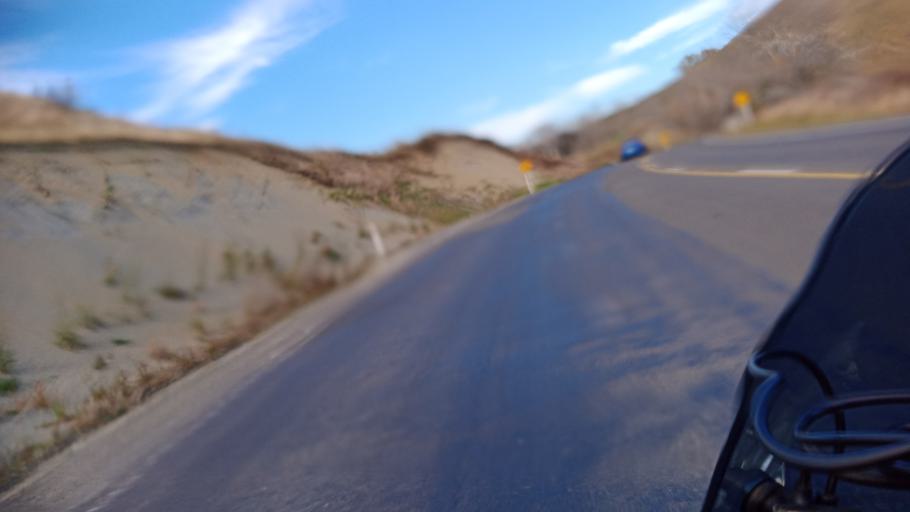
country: NZ
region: Gisborne
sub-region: Gisborne District
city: Gisborne
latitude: -38.8228
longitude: 177.9050
